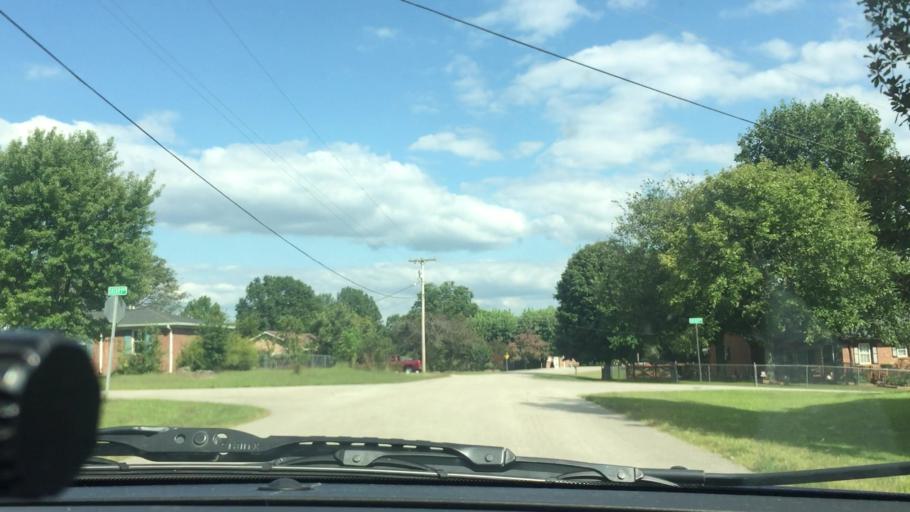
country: US
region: Tennessee
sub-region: Maury County
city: Columbia
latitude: 35.6817
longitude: -86.9884
